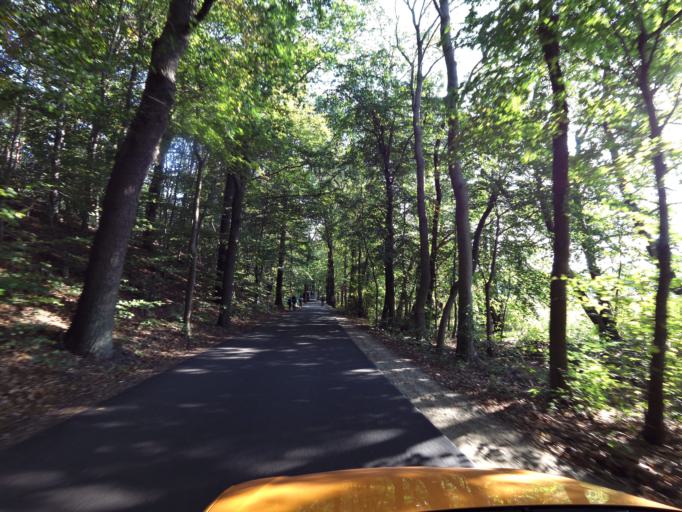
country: DE
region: Brandenburg
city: Potsdam
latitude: 52.4478
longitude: 13.0684
